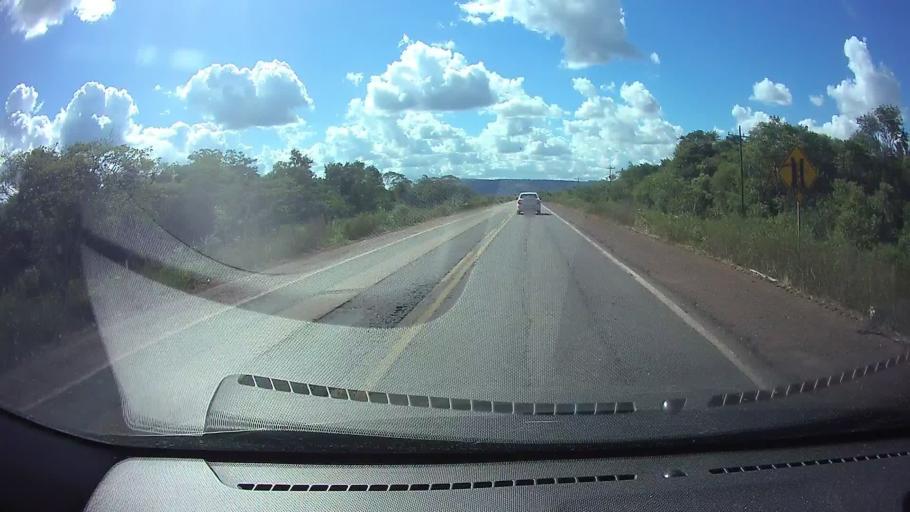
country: PY
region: Paraguari
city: Sapucai
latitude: -25.7167
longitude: -56.8349
